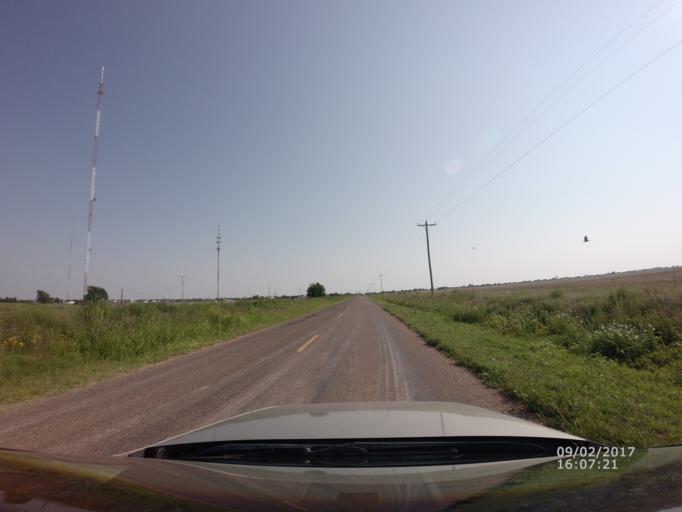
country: US
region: New Mexico
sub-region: Curry County
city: Clovis
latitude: 34.4407
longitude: -103.2141
